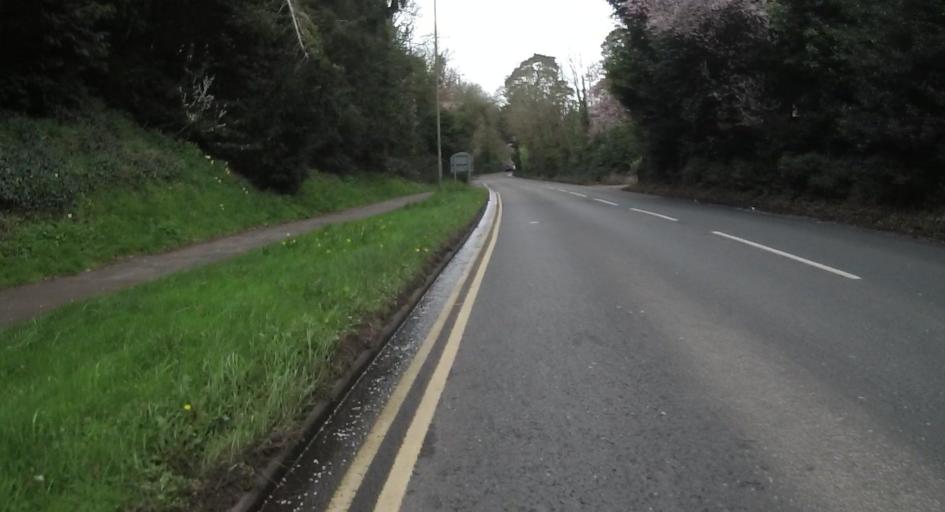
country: GB
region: England
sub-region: Surrey
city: Farnham
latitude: 51.1998
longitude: -0.7920
